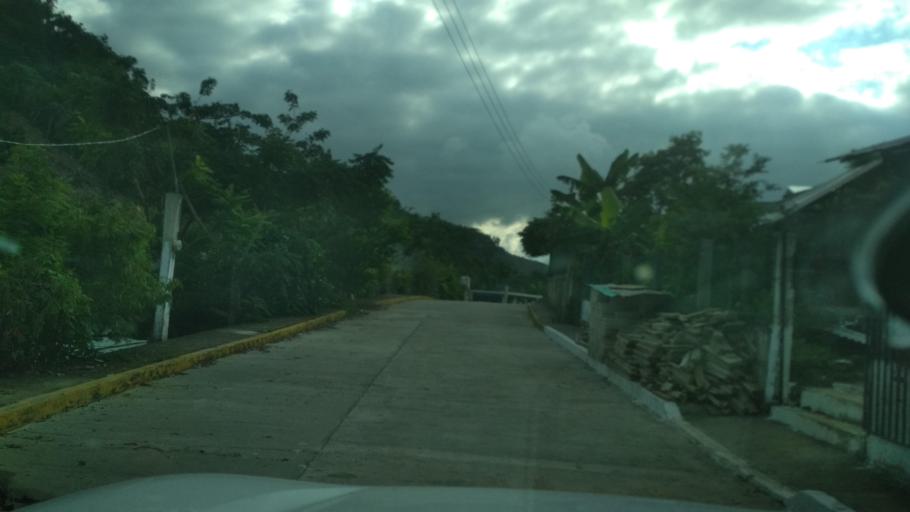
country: MX
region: Veracruz
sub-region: Papantla
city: Polutla
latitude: 20.5714
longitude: -97.2539
